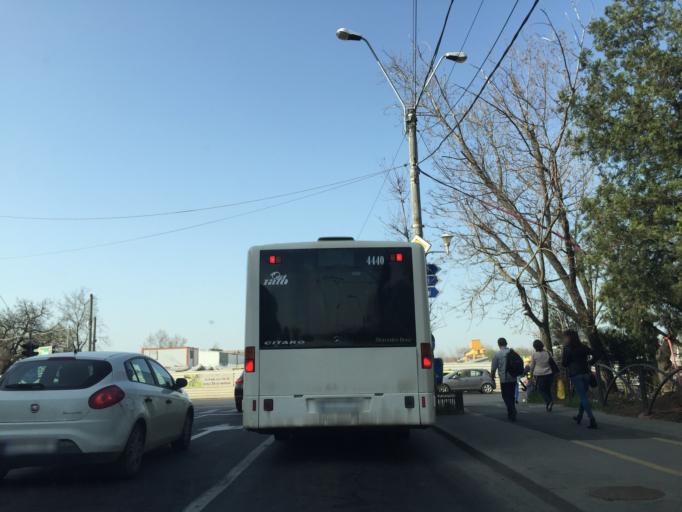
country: RO
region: Bucuresti
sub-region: Municipiul Bucuresti
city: Bucuresti
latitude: 44.4295
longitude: 26.0640
